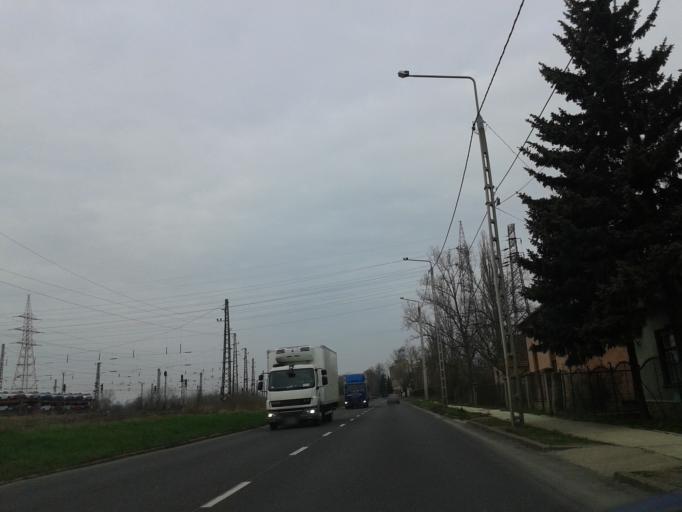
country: HU
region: Komarom-Esztergom
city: Almasfuzito
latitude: 47.7275
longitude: 18.2564
